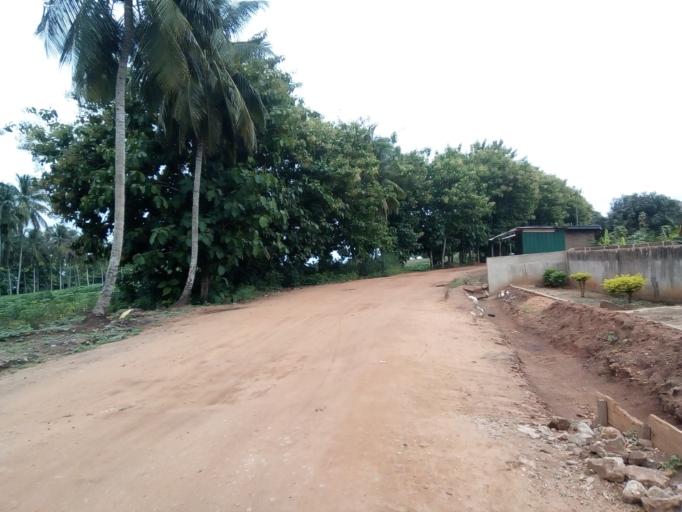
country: GH
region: Eastern
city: Nsawam
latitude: 5.7779
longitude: -0.3398
